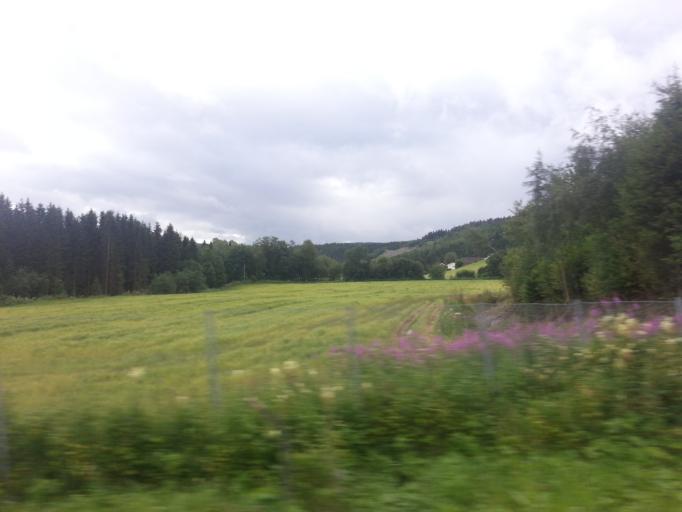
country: NO
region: Sor-Trondelag
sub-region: Malvik
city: Malvik
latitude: 63.4220
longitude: 10.6175
